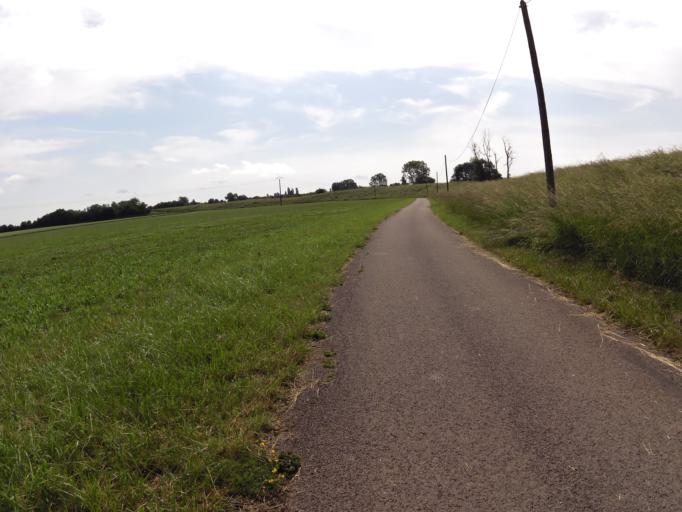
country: FR
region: Champagne-Ardenne
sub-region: Departement de l'Aube
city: Lusigny-sur-Barse
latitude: 48.2665
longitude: 4.2220
